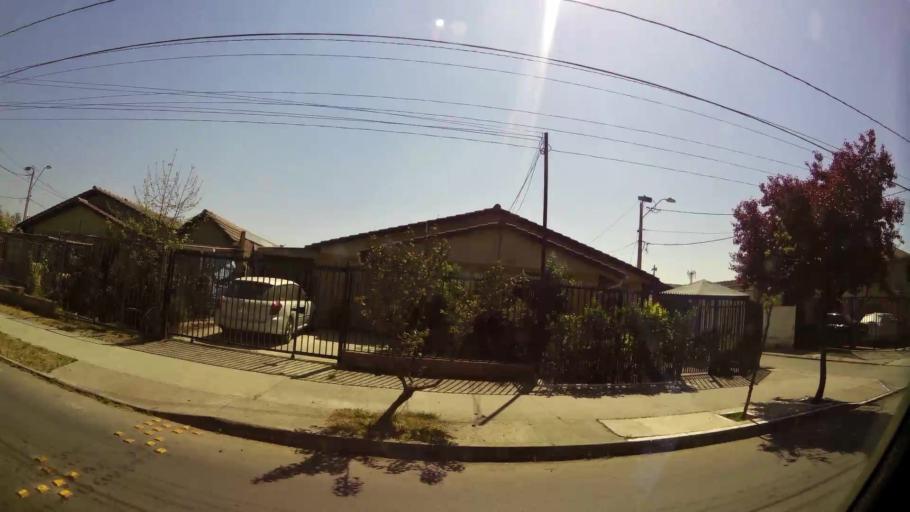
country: CL
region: Santiago Metropolitan
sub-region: Provincia de Talagante
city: Penaflor
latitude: -33.5713
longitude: -70.8131
